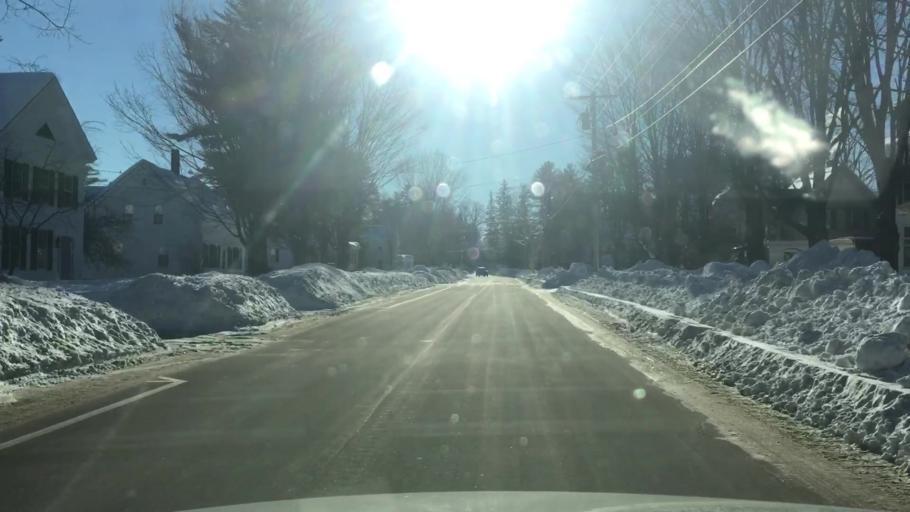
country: US
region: Maine
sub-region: Oxford County
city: Bethel
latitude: 44.4025
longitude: -70.7894
